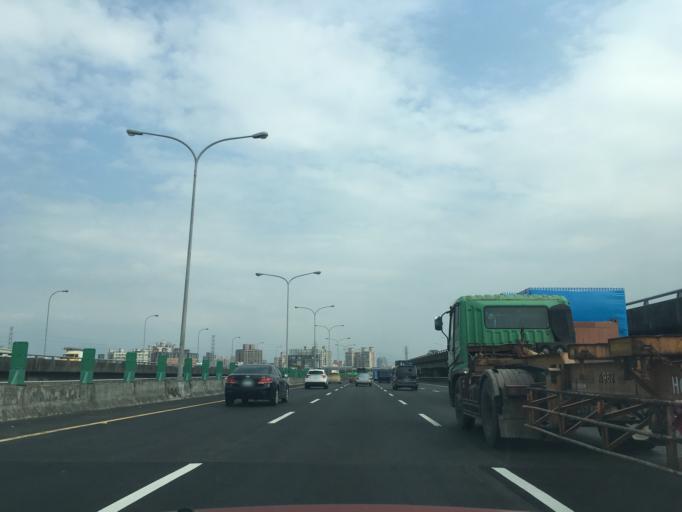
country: TW
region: Taipei
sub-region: Taipei
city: Banqiao
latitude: 25.0738
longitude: 121.4569
